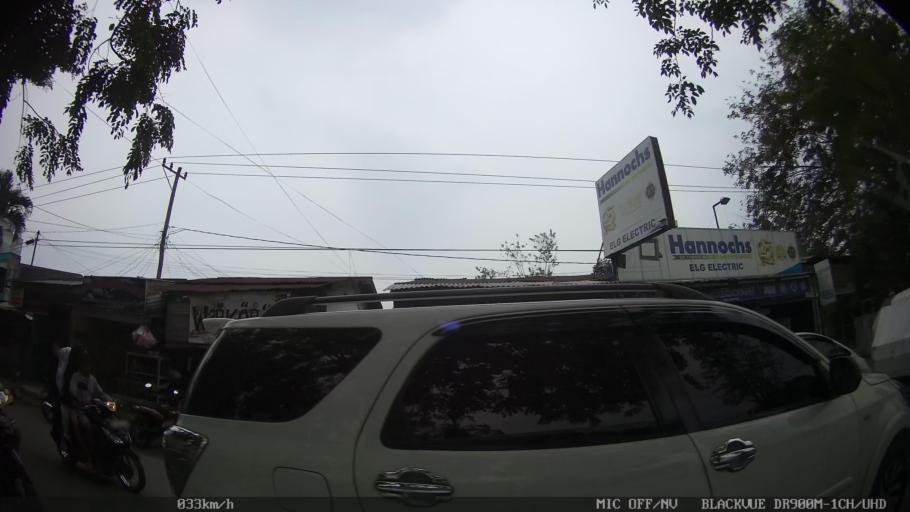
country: ID
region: North Sumatra
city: Medan
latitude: 3.5582
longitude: 98.7030
